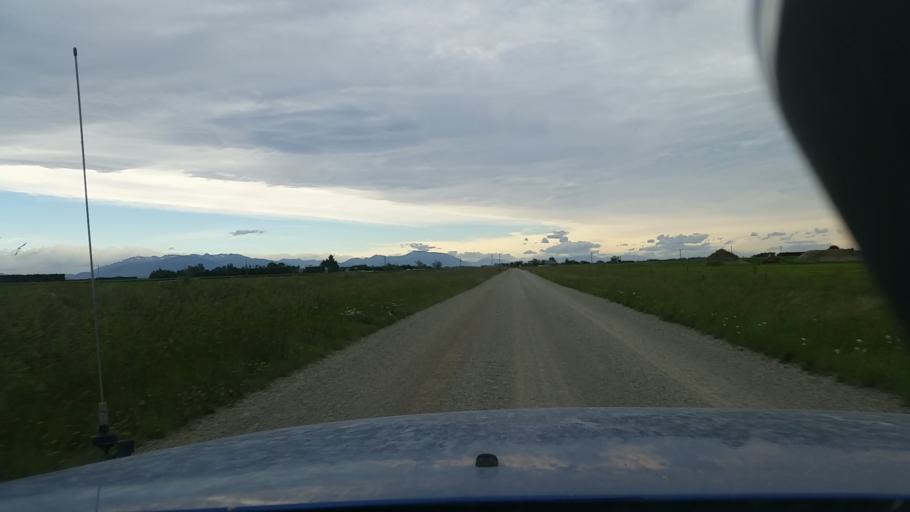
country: NZ
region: Canterbury
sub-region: Ashburton District
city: Tinwald
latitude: -43.9799
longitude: 171.5076
